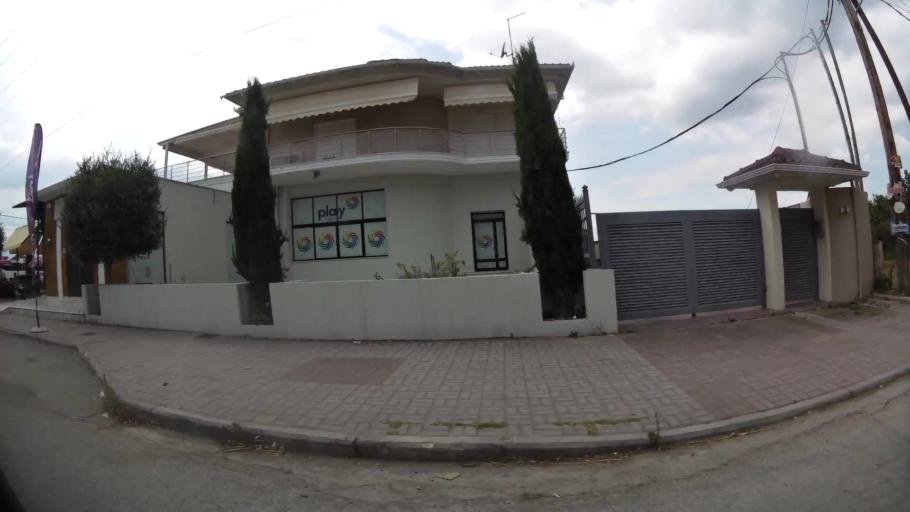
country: GR
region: Central Macedonia
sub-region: Nomos Pierias
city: Paralia
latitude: 40.2690
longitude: 22.5936
